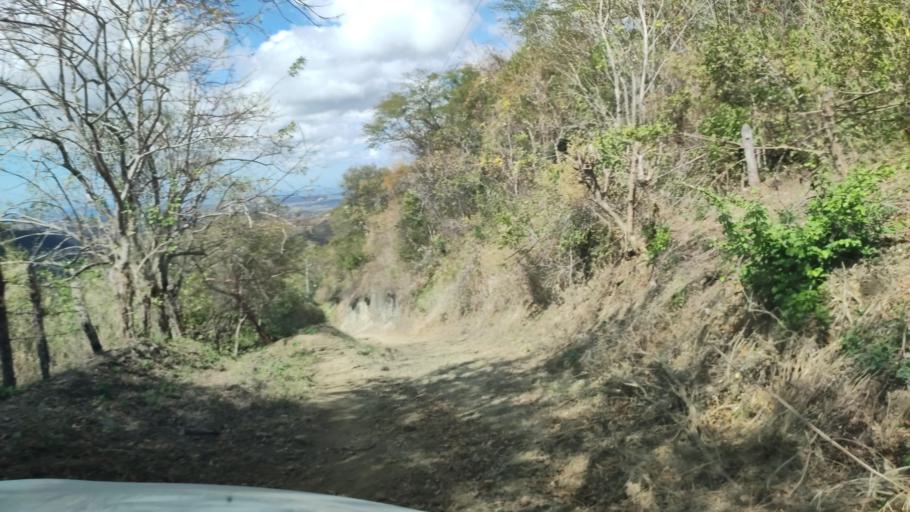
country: NI
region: Carazo
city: Santa Teresa
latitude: 11.6522
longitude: -86.2030
